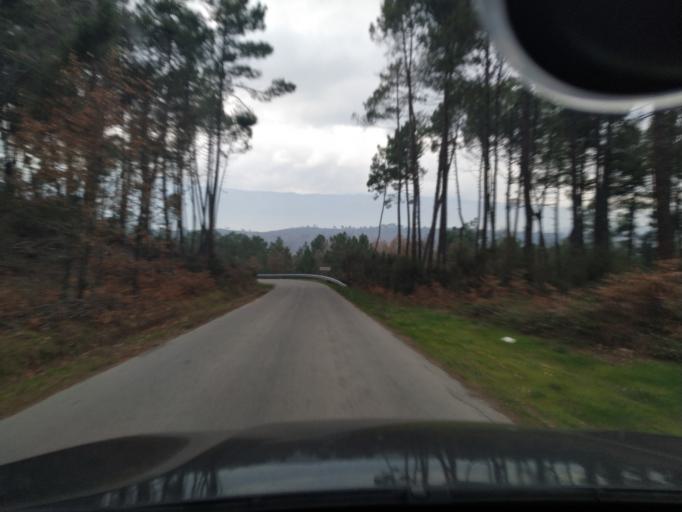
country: PT
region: Vila Real
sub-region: Vila Real
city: Vila Real
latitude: 41.3379
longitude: -7.6562
